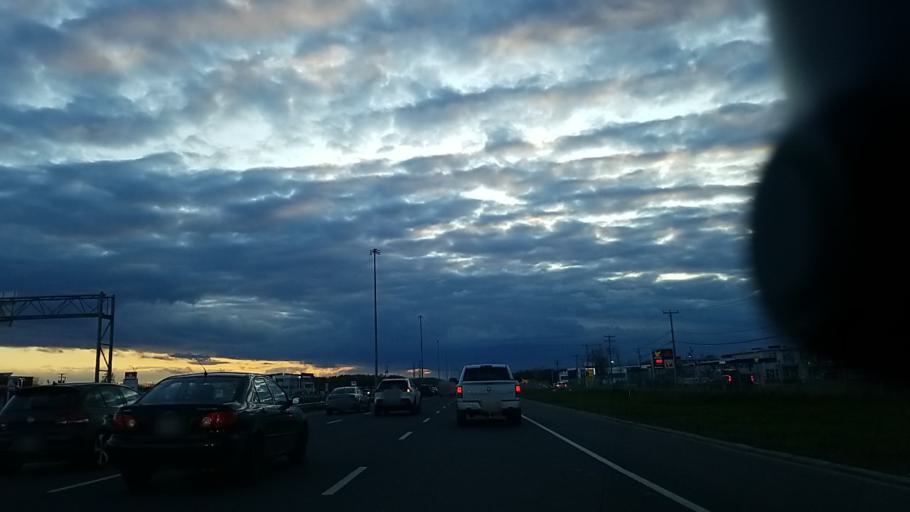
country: CA
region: Quebec
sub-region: Laurentides
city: Boisbriand
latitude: 45.5607
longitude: -73.7892
